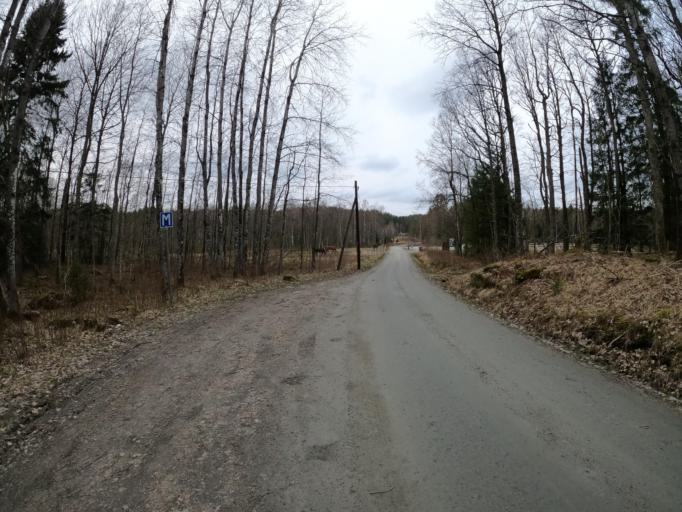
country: SE
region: Vaestra Goetaland
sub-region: Harryda Kommun
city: Molnlycke
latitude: 57.6323
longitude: 12.1035
